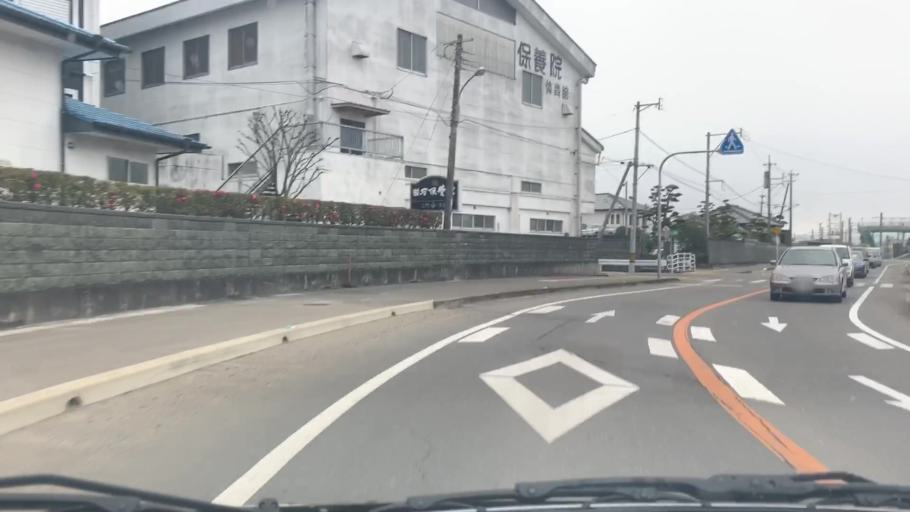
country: JP
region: Saga Prefecture
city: Kashima
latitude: 33.1890
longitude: 130.1361
